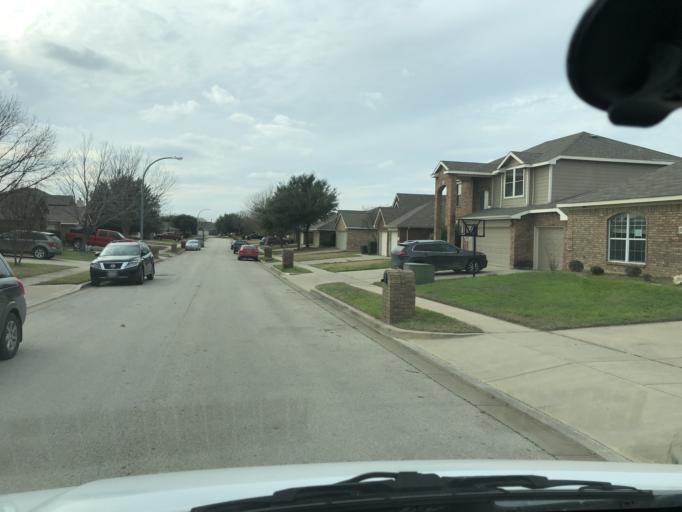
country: US
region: Texas
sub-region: Tarrant County
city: Saginaw
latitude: 32.9088
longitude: -97.3708
